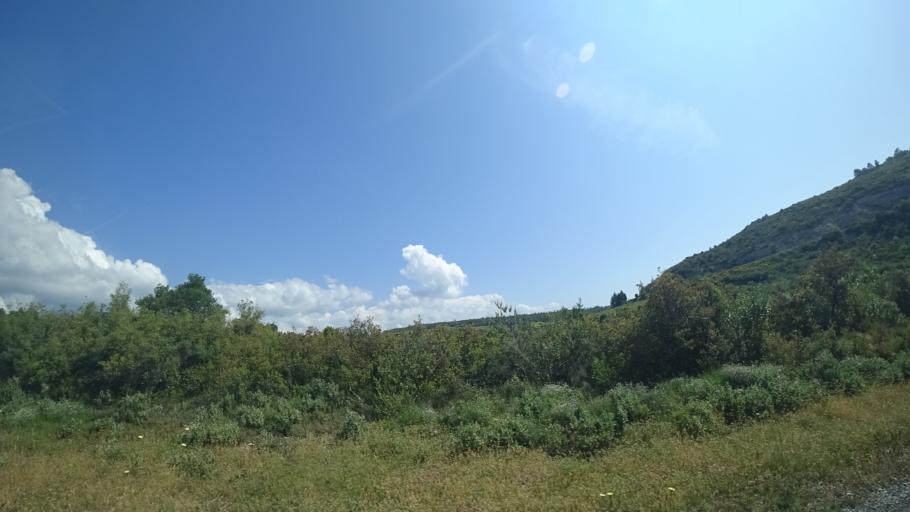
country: FR
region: Languedoc-Roussillon
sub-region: Departement de l'Herault
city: Olonzac
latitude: 43.3523
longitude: 2.7400
